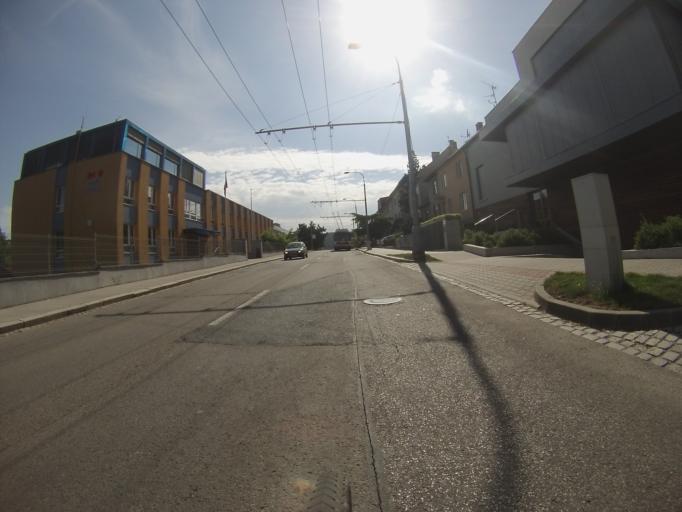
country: CZ
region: South Moravian
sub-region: Mesto Brno
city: Brno
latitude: 49.2165
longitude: 16.5674
